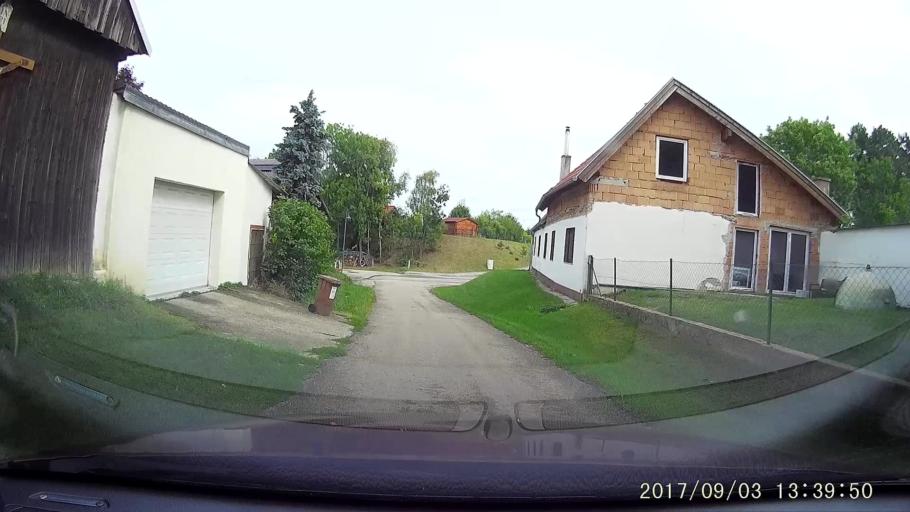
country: AT
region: Lower Austria
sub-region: Politischer Bezirk Hollabrunn
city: Wullersdorf
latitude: 48.5992
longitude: 16.0687
